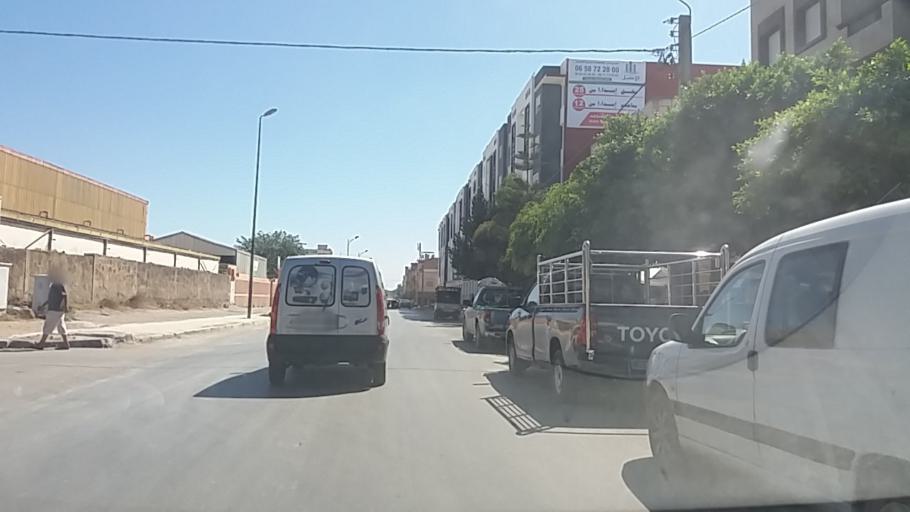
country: MA
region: Gharb-Chrarda-Beni Hssen
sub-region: Kenitra Province
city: Kenitra
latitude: 34.2407
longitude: -6.6152
